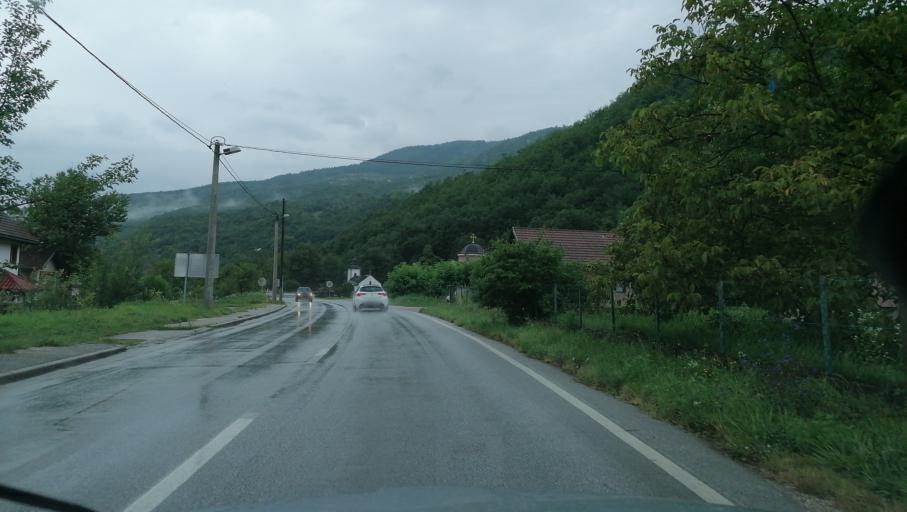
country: BA
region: Federation of Bosnia and Herzegovina
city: Gorazde
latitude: 43.6829
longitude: 19.0044
